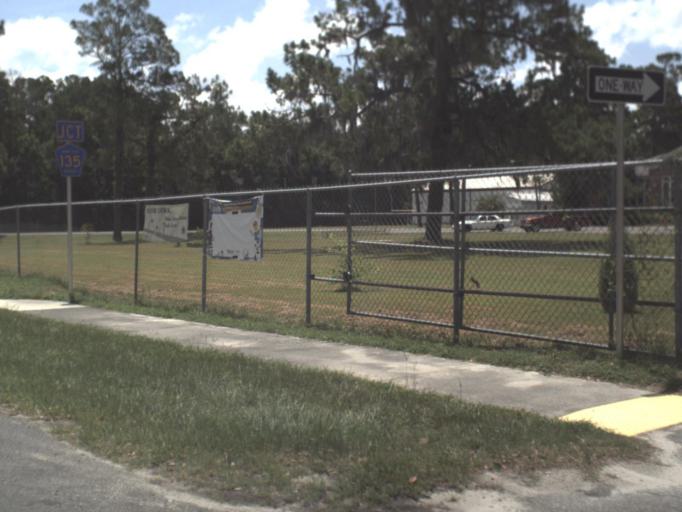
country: US
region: Florida
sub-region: Suwannee County
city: Wellborn
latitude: 30.3299
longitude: -82.7536
